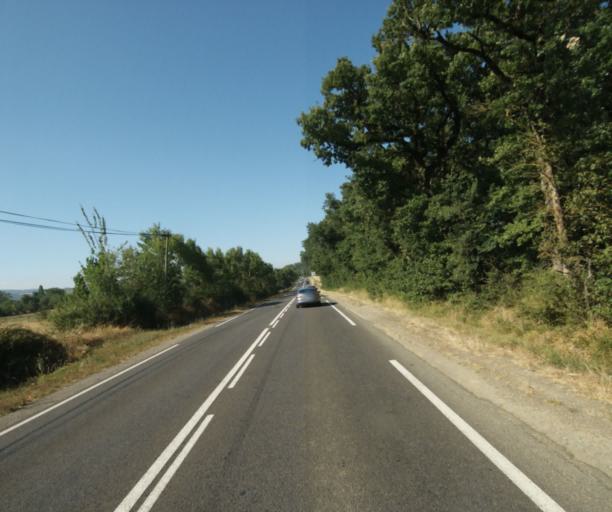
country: FR
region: Midi-Pyrenees
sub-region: Departement de la Haute-Garonne
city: Revel
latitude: 43.4800
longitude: 2.0203
